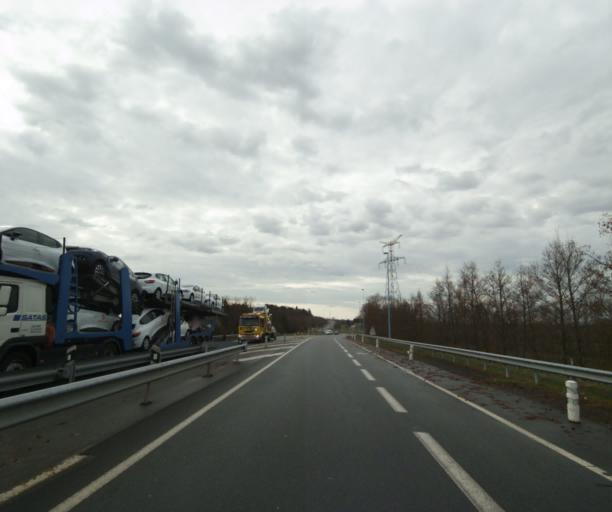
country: FR
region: Auvergne
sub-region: Departement de l'Allier
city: Toulon-sur-Allier
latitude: 46.5273
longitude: 3.3521
